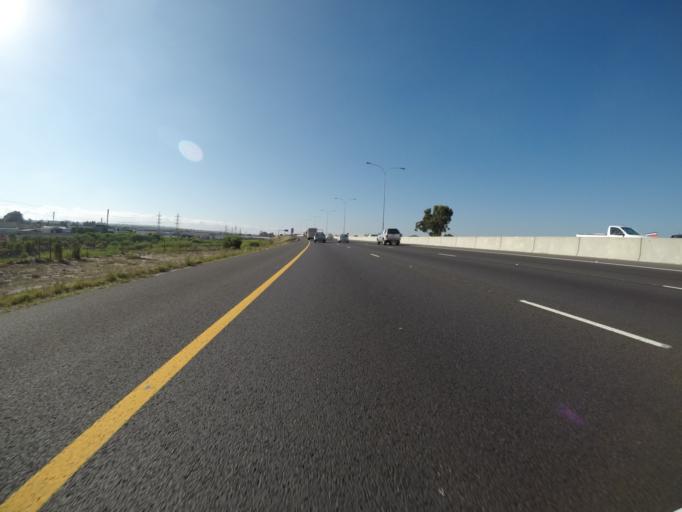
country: ZA
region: Western Cape
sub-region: City of Cape Town
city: Kraaifontein
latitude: -33.8948
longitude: 18.6775
